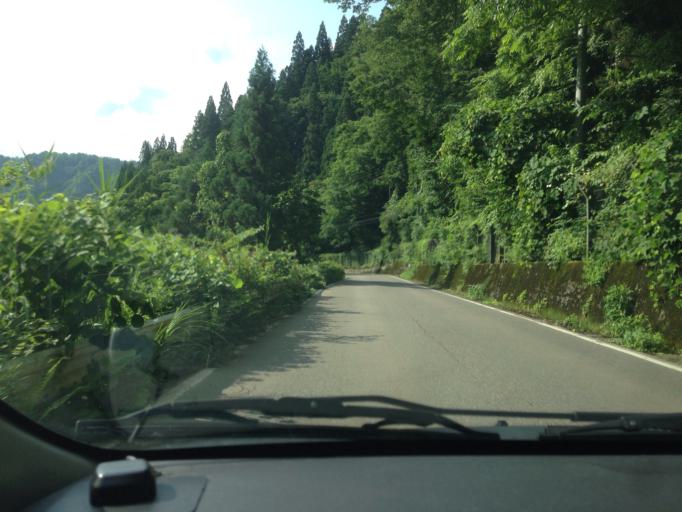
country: JP
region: Fukushima
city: Kitakata
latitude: 37.4490
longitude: 139.5263
